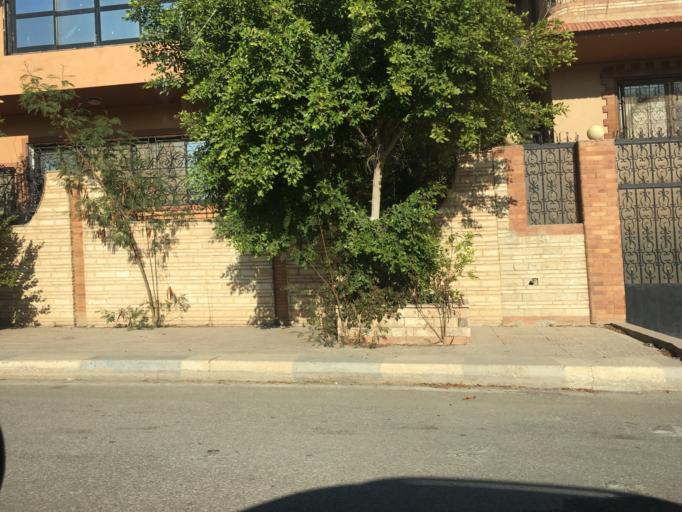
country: EG
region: Al Jizah
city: Madinat Sittah Uktubar
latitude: 29.9876
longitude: 30.9418
